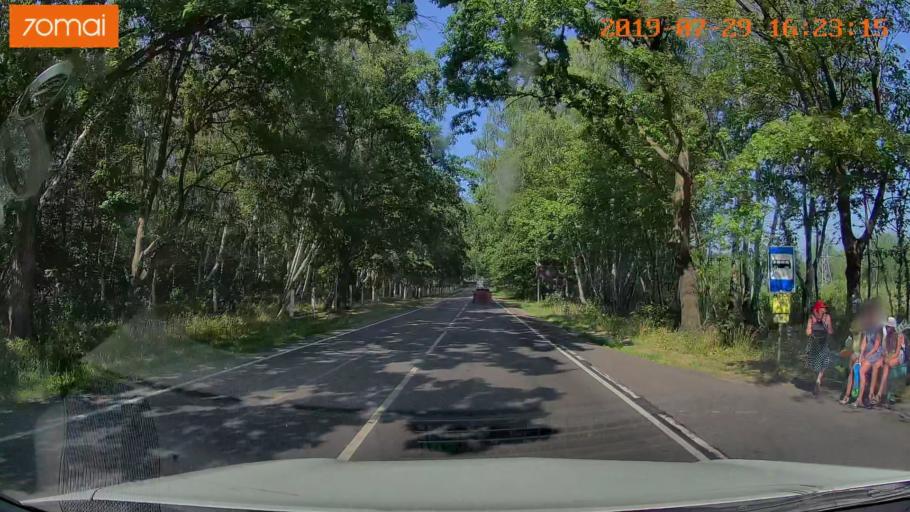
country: RU
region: Kaliningrad
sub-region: Gorod Kaliningrad
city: Baltiysk
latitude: 54.7043
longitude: 19.9450
